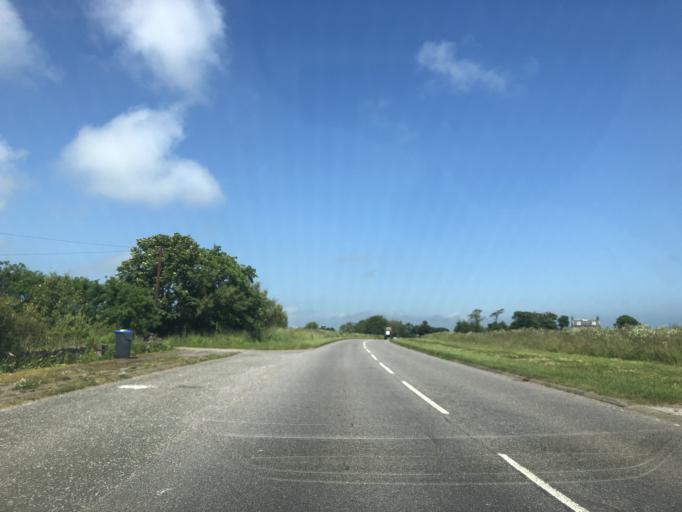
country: GB
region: Scotland
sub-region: Aberdeenshire
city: Stonehaven
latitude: 56.9312
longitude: -2.2078
